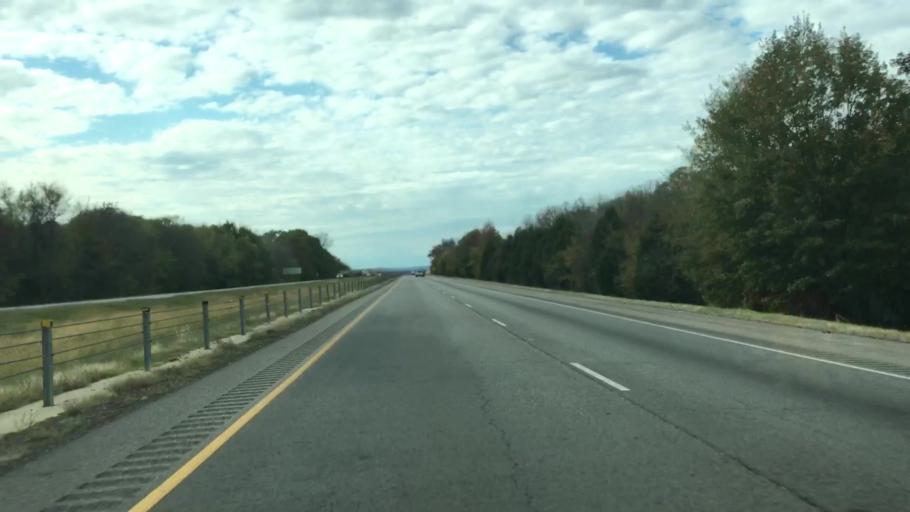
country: US
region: Arkansas
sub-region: Conway County
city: Morrilton
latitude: 35.1827
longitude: -92.7649
